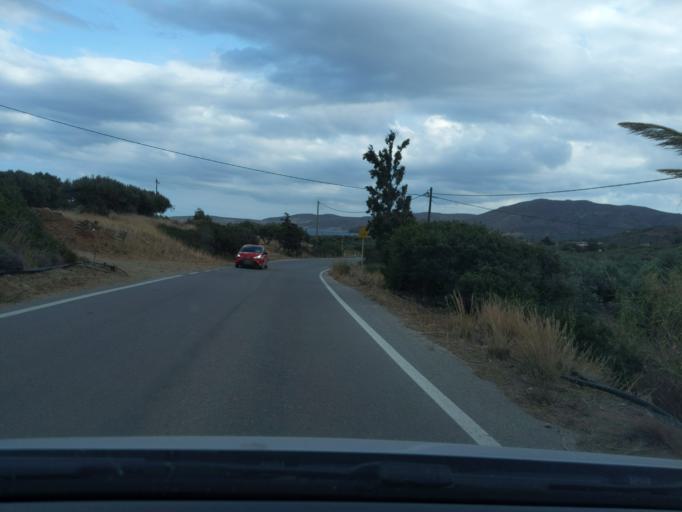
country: GR
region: Crete
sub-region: Nomos Lasithiou
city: Palekastro
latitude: 35.2172
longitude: 26.2637
